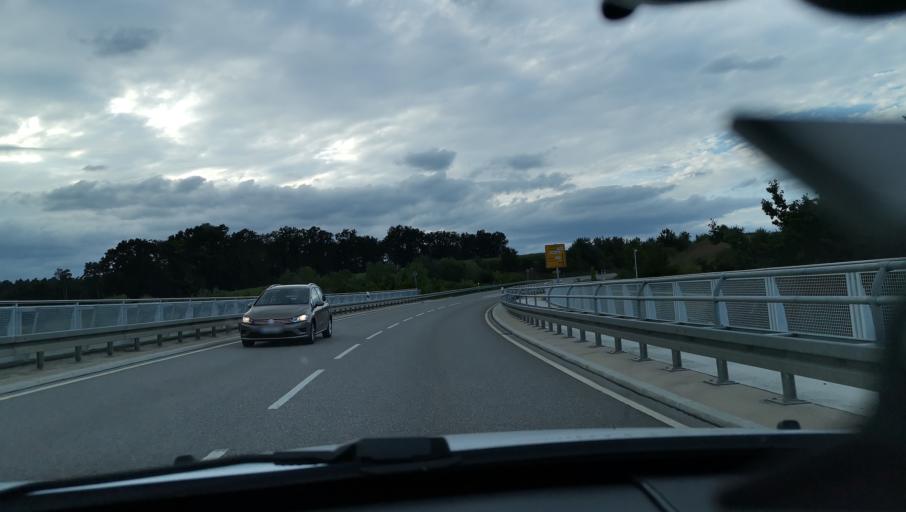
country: DE
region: Bavaria
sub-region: Regierungsbezirk Mittelfranken
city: Zirndorf
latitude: 49.4358
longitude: 10.9394
